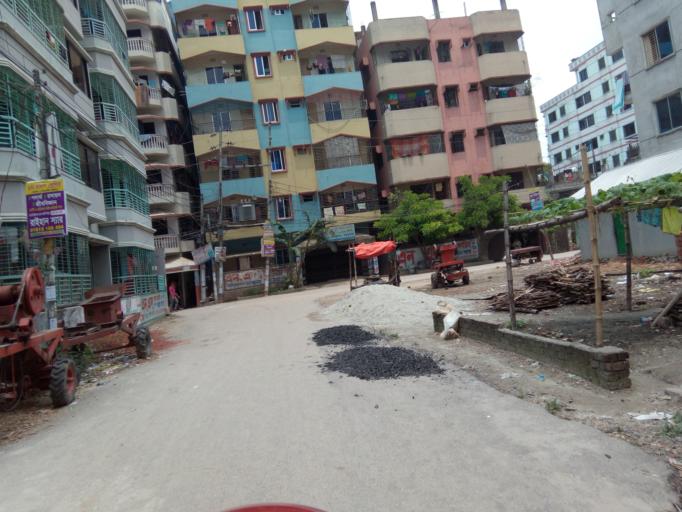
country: BD
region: Dhaka
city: Paltan
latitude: 23.7531
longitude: 90.4399
